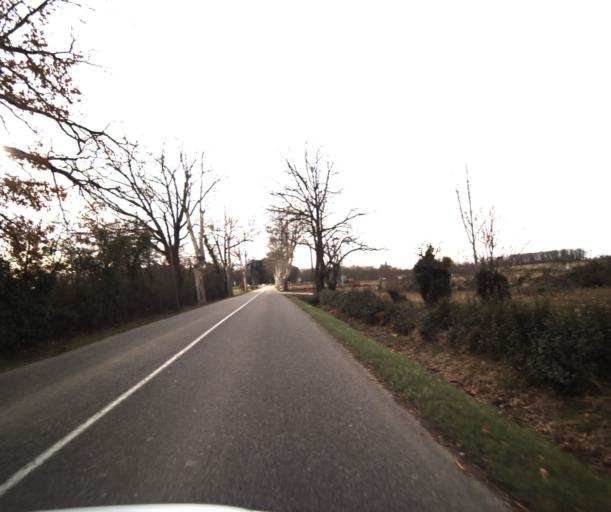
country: FR
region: Midi-Pyrenees
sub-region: Departement du Tarn-et-Garonne
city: Campsas
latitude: 43.8992
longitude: 1.3114
